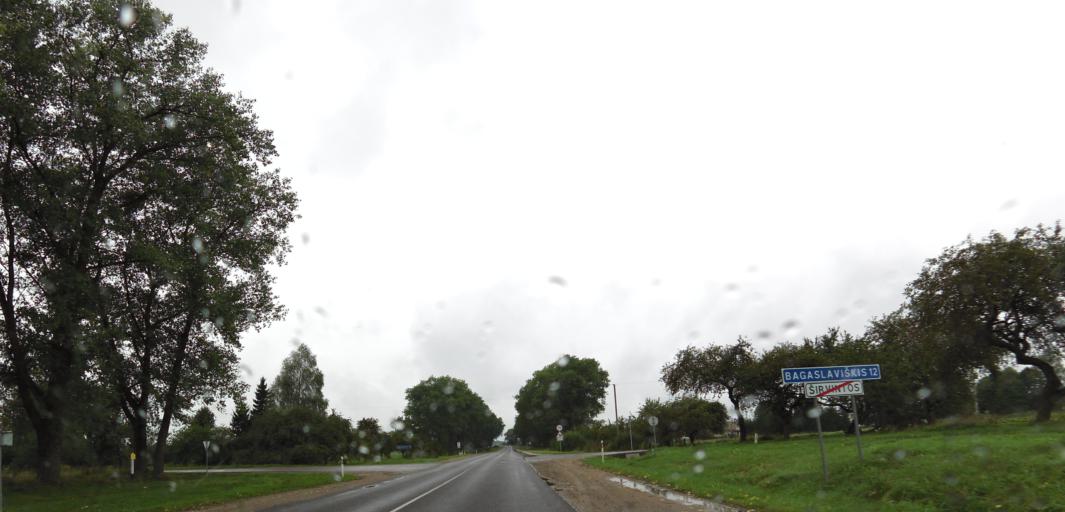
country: LT
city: Sirvintos
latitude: 55.0482
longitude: 24.9362
